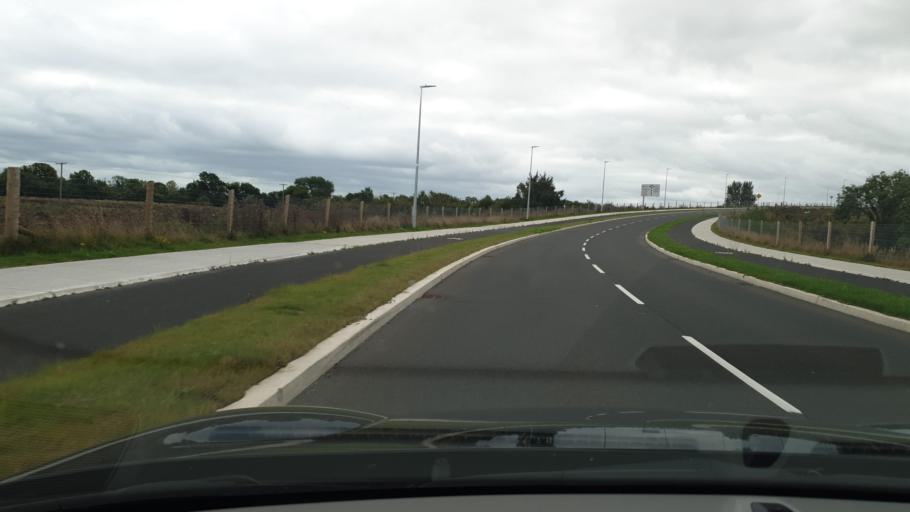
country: IE
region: Leinster
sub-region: Kildare
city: Sallins
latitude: 53.2501
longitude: -6.6772
